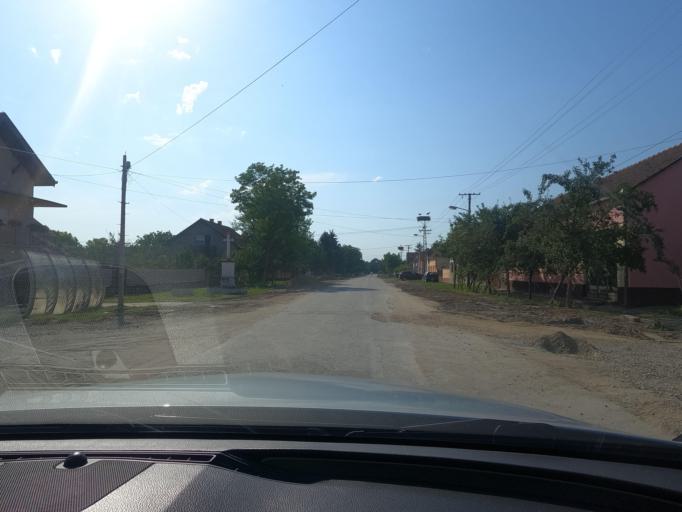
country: RS
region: Autonomna Pokrajina Vojvodina
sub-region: Juznobacki Okrug
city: Kovilj
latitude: 45.2183
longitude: 20.0244
